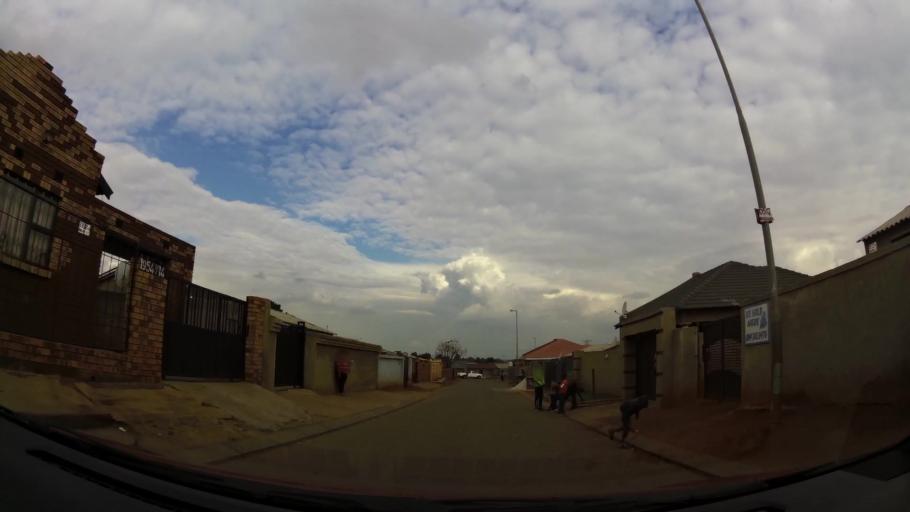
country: ZA
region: Gauteng
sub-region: City of Johannesburg Metropolitan Municipality
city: Soweto
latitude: -26.2452
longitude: 27.8368
